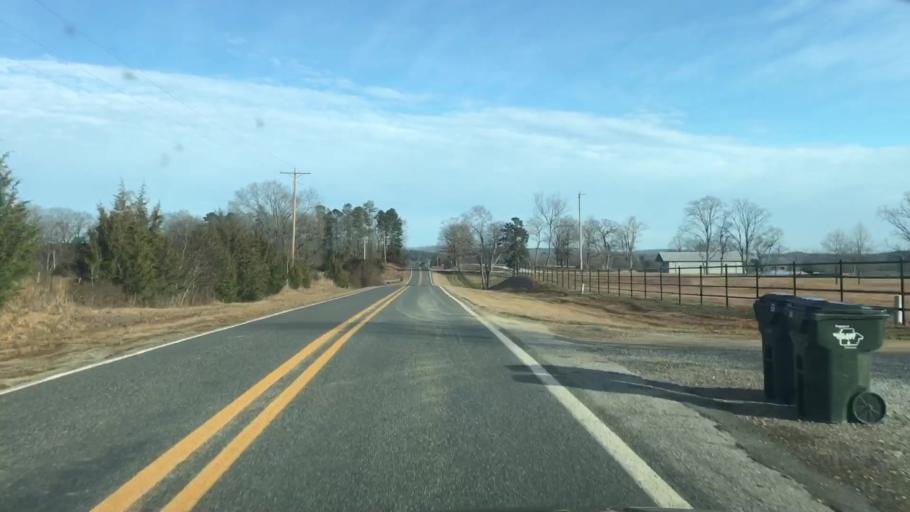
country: US
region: Arkansas
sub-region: Garland County
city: Rockwell
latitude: 34.5000
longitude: -93.2764
